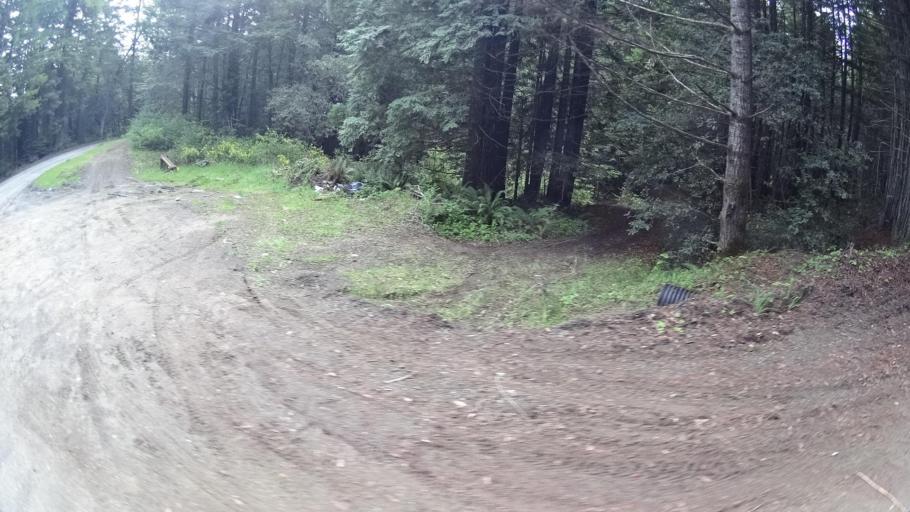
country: US
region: California
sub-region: Humboldt County
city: Redway
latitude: 40.3166
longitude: -123.8314
